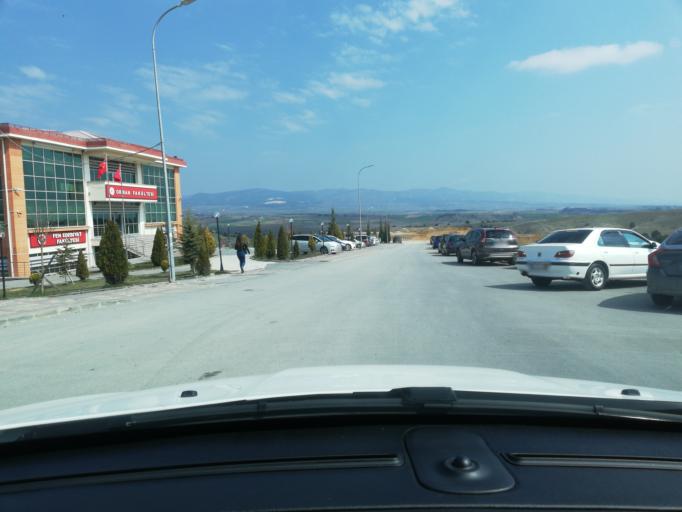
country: TR
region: Kastamonu
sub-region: Cide
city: Kastamonu
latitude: 41.4369
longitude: 33.7667
